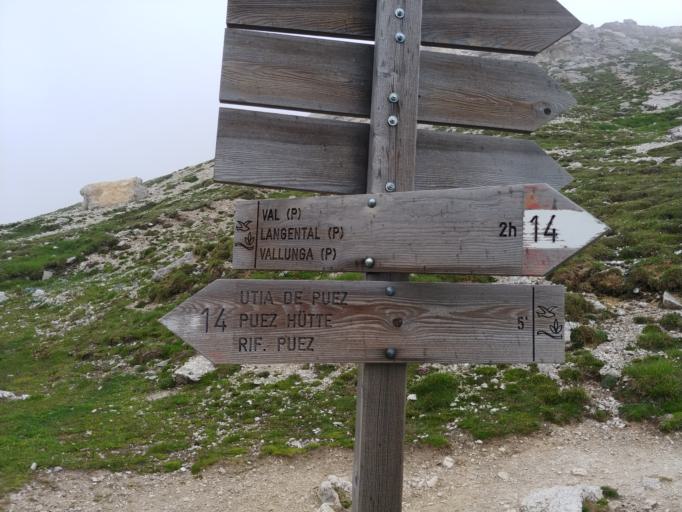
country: IT
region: Trentino-Alto Adige
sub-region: Bolzano
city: Corvara in Badia
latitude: 46.5895
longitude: 11.8297
